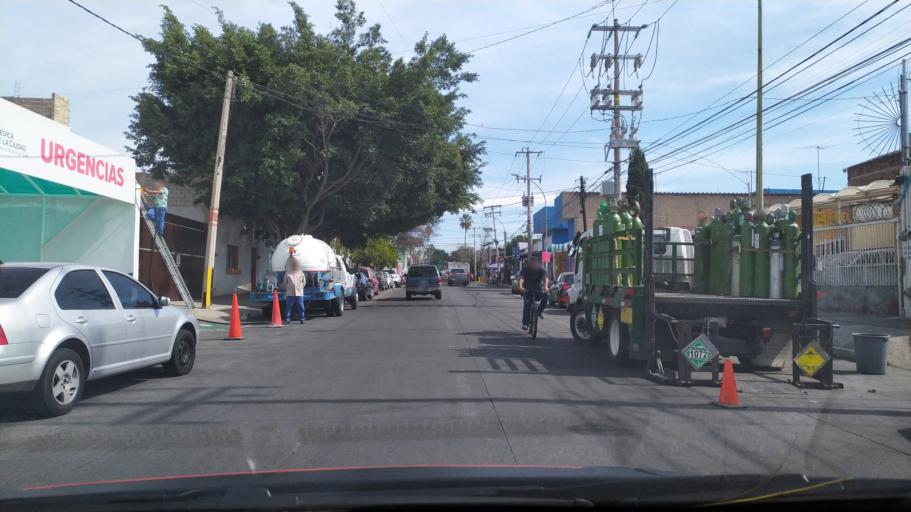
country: MX
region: Jalisco
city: Tlaquepaque
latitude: 20.6818
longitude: -103.3283
